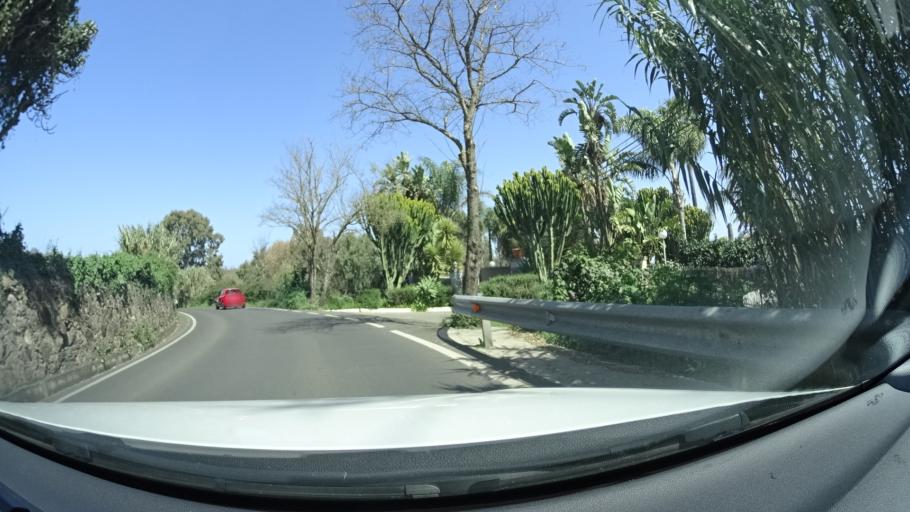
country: ES
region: Canary Islands
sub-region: Provincia de Las Palmas
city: Teror
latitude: 28.0701
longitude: -15.5405
